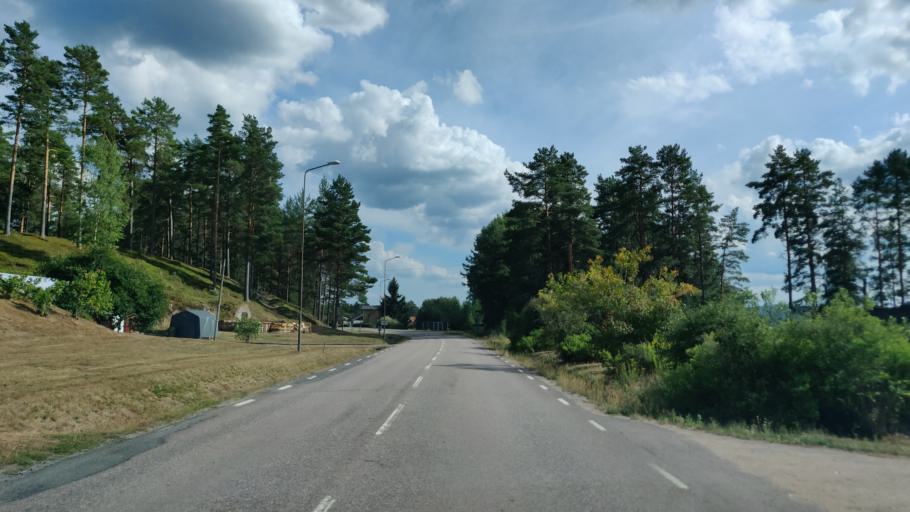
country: SE
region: Vaermland
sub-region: Hagfors Kommun
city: Ekshaerad
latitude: 60.1154
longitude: 13.5632
